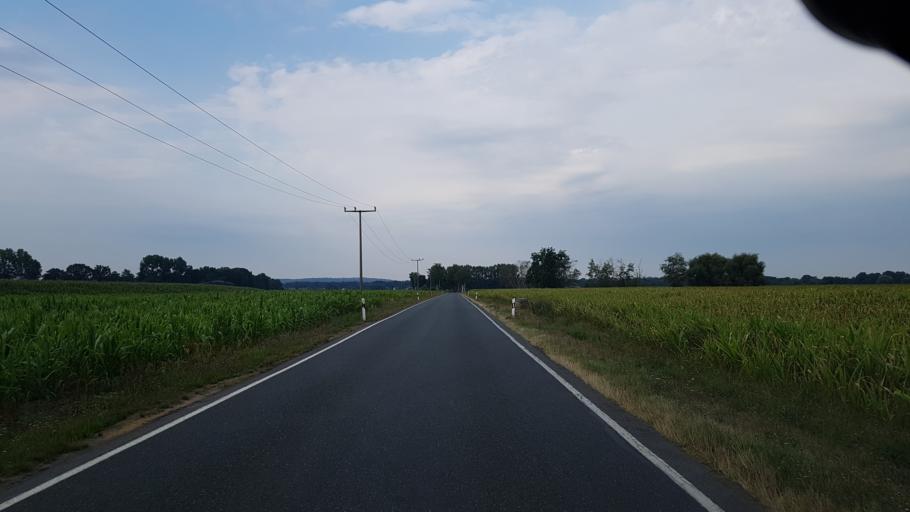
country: DE
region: Brandenburg
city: Lindenau
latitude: 51.4161
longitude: 13.7260
